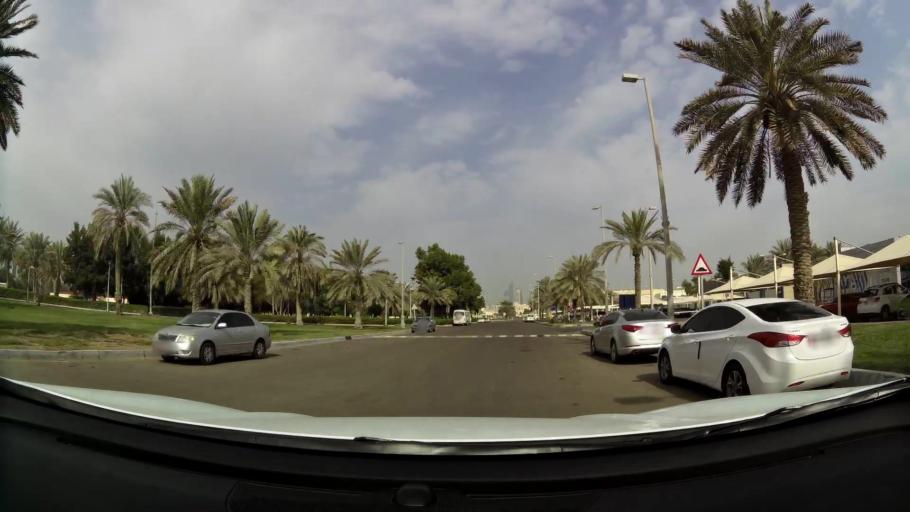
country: AE
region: Abu Dhabi
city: Abu Dhabi
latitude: 24.4555
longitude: 54.3882
